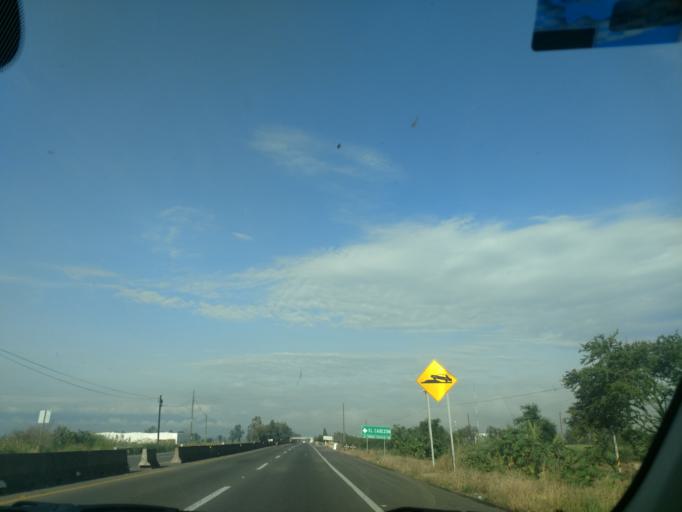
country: MX
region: Jalisco
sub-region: Ameca
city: Los Pocitos
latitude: 20.5350
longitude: -103.9592
